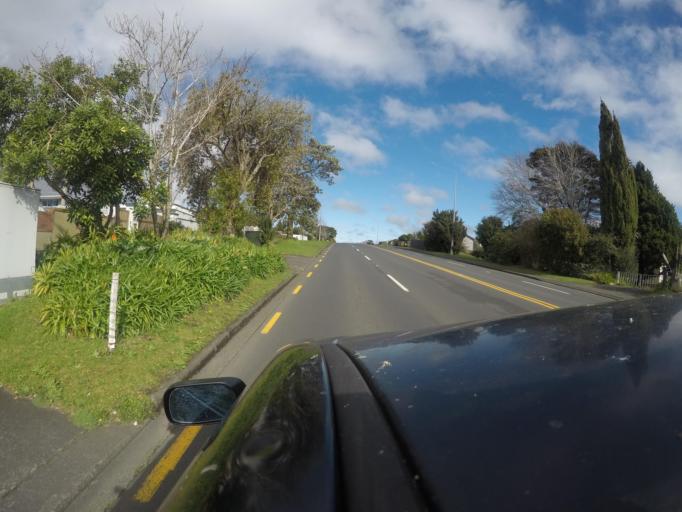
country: NZ
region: Auckland
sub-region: Auckland
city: Rosebank
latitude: -36.8907
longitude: 174.6448
